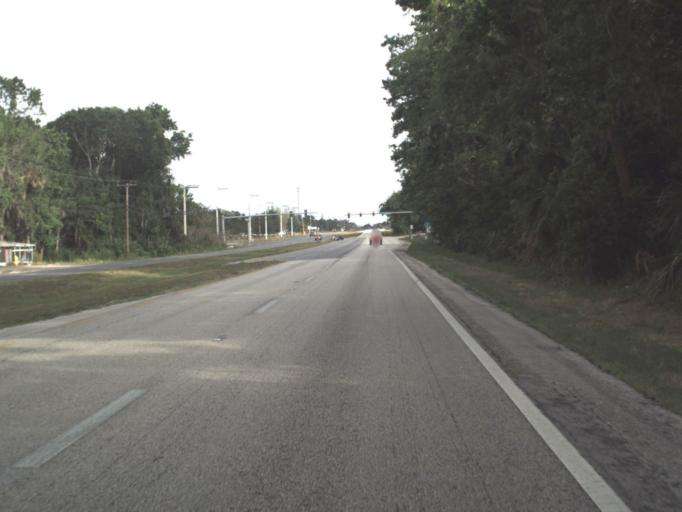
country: US
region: Florida
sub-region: Brevard County
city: Mims
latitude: 28.6423
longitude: -80.8332
